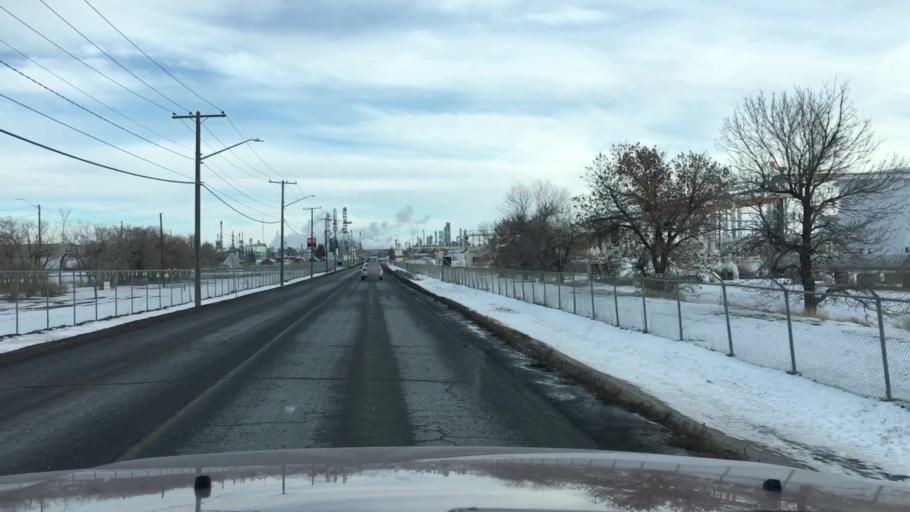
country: CA
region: Saskatchewan
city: Regina
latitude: 50.4843
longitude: -104.5913
